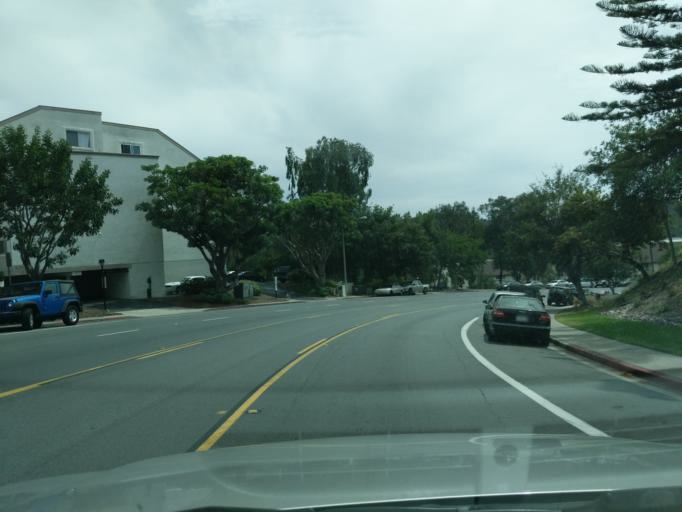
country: US
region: California
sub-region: San Diego County
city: San Diego
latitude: 32.7874
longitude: -117.1082
